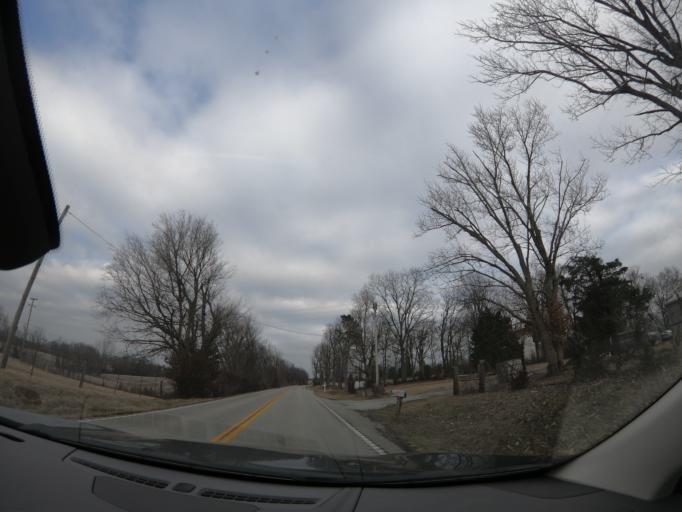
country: US
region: Kentucky
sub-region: Nelson County
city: Bardstown
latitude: 37.8500
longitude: -85.3577
